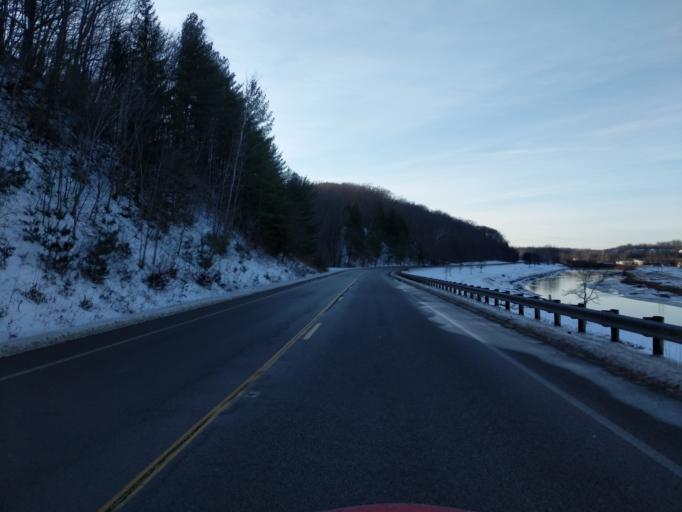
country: US
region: Ohio
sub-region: Athens County
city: Athens
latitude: 39.3252
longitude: -82.1151
